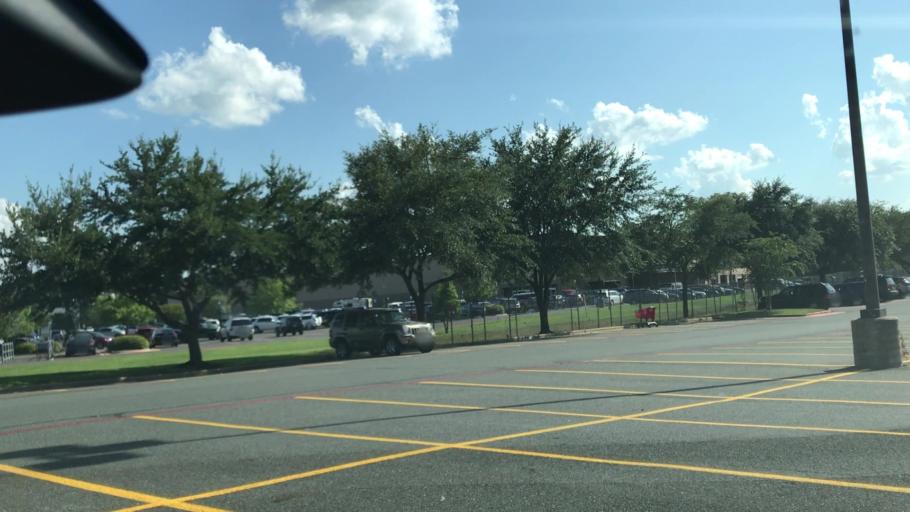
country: US
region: Louisiana
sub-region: Bossier Parish
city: Bossier City
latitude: 32.4396
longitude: -93.7183
